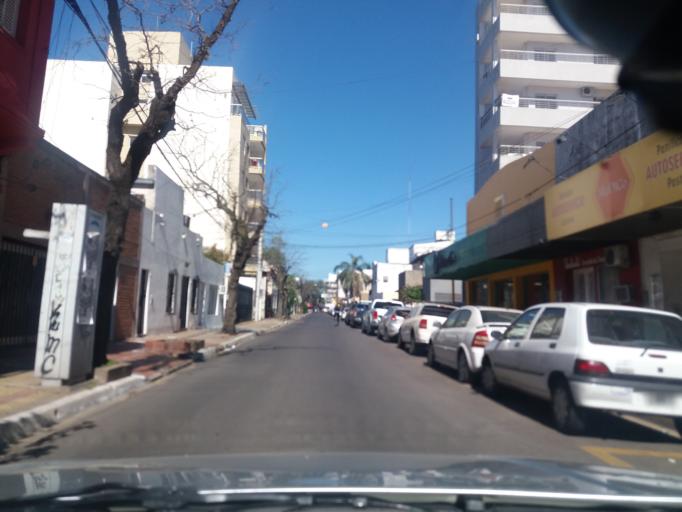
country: AR
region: Corrientes
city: Corrientes
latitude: -27.4733
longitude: -58.8395
